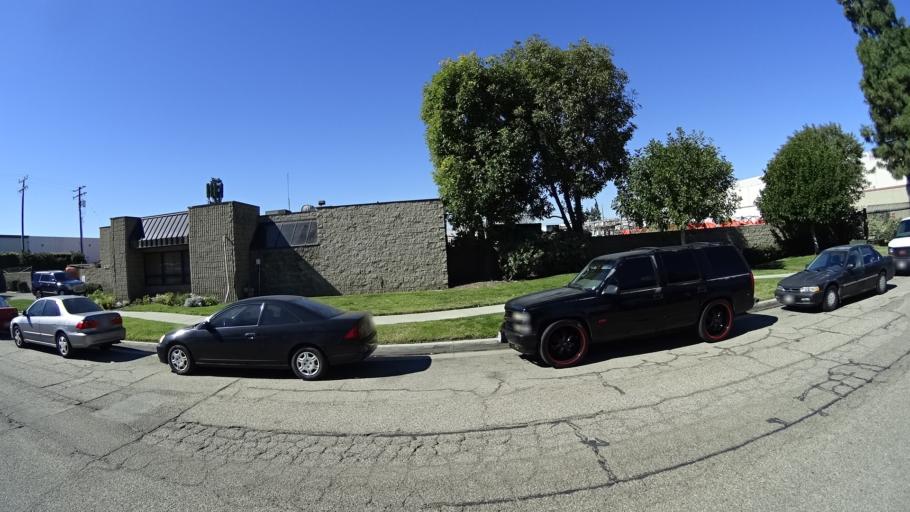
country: US
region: California
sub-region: Orange County
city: Yorba Linda
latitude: 33.8650
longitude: -117.8234
